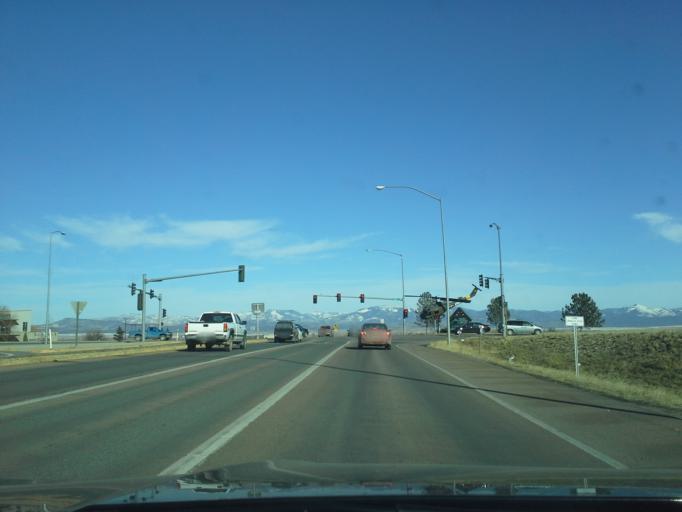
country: US
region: Montana
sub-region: Lewis and Clark County
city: Helena
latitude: 46.6057
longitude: -112.0051
